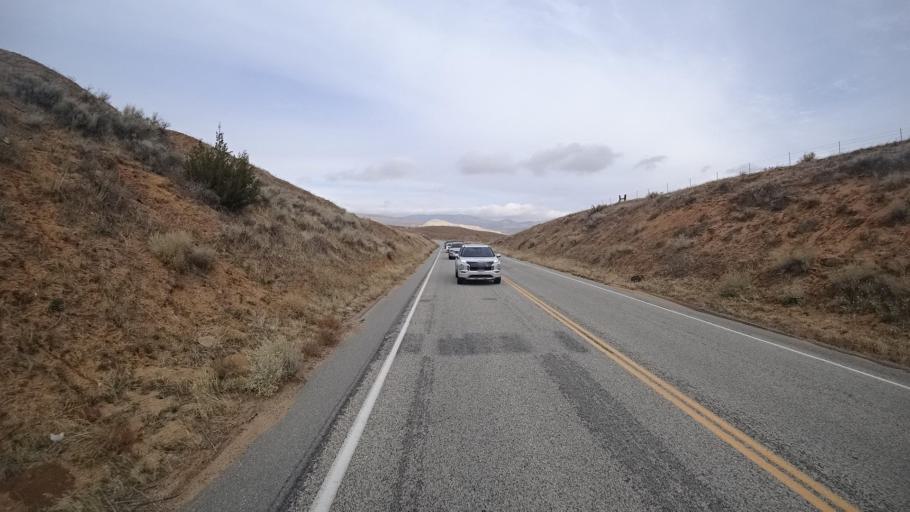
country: US
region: California
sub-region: Kern County
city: Tehachapi
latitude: 35.0846
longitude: -118.3951
